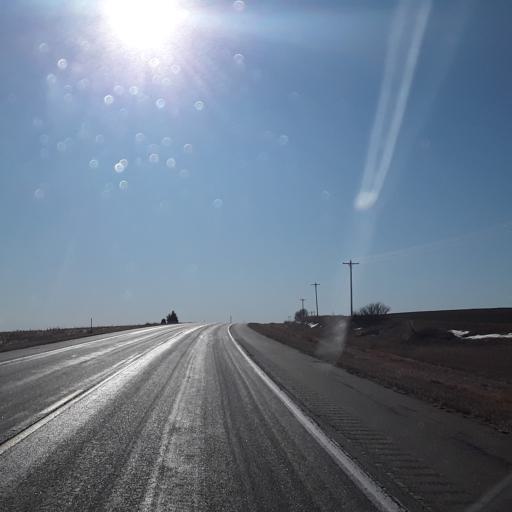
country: US
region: Nebraska
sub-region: Frontier County
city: Stockville
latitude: 40.5610
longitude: -100.6313
